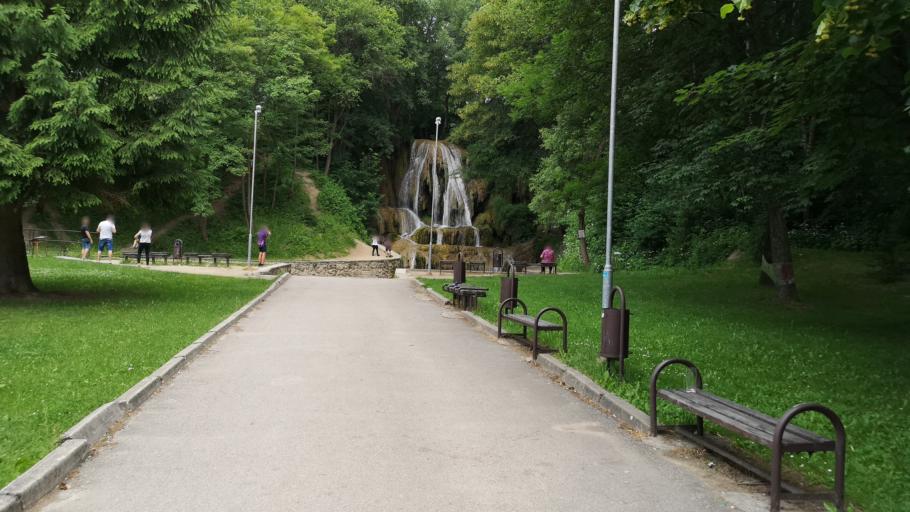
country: SK
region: Zilinsky
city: Ruzomberok
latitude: 49.1292
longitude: 19.4036
